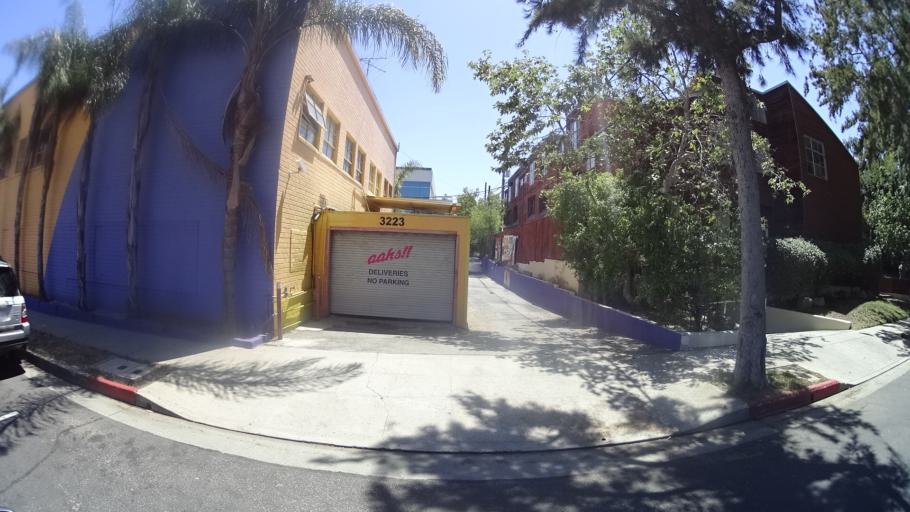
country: US
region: California
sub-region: Los Angeles County
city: Santa Monica
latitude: 34.0415
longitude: -118.4716
